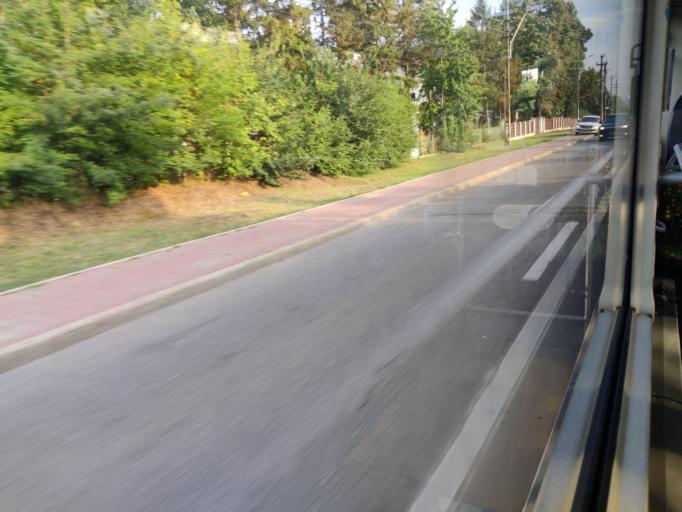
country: RO
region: Iasi
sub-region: Municipiul Iasi
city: Iasi
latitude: 47.1766
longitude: 27.5982
